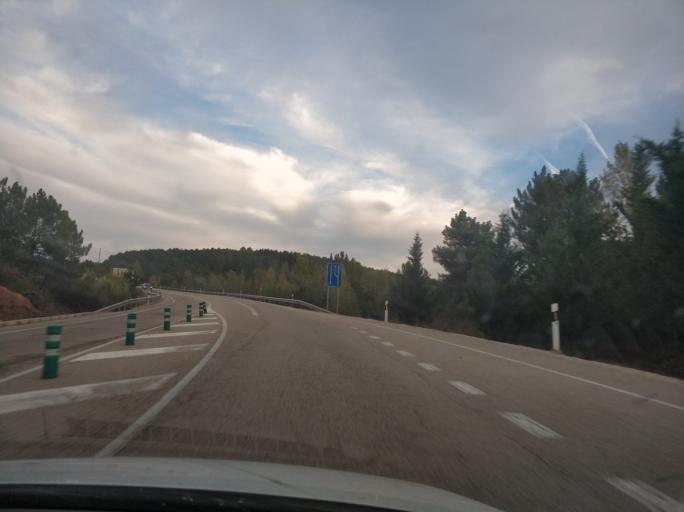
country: ES
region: Castille and Leon
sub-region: Provincia de Burgos
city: Pinilla de los Barruecos
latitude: 41.9058
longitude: -3.2765
